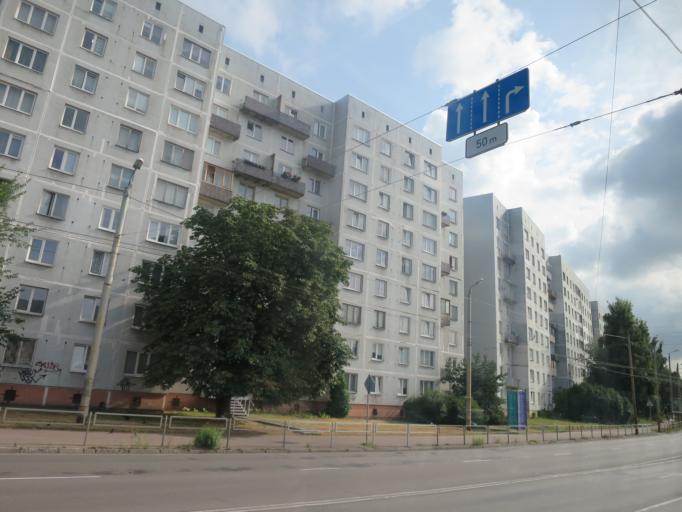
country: LV
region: Riga
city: Riga
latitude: 56.9599
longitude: 24.1762
